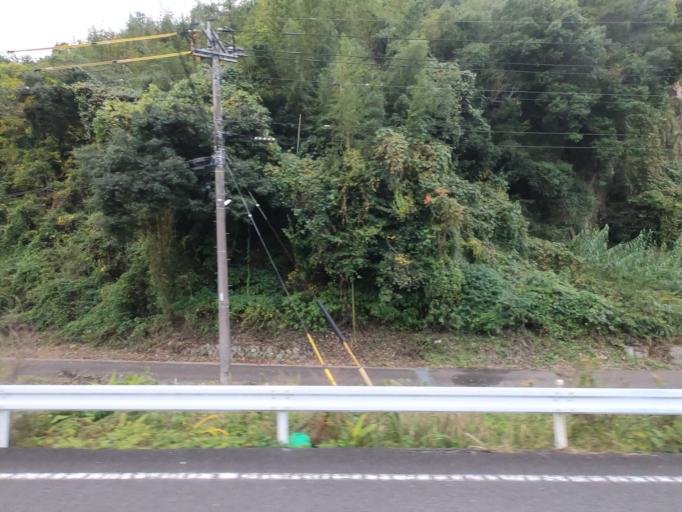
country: JP
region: Kumamoto
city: Minamata
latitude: 32.2653
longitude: 130.5068
